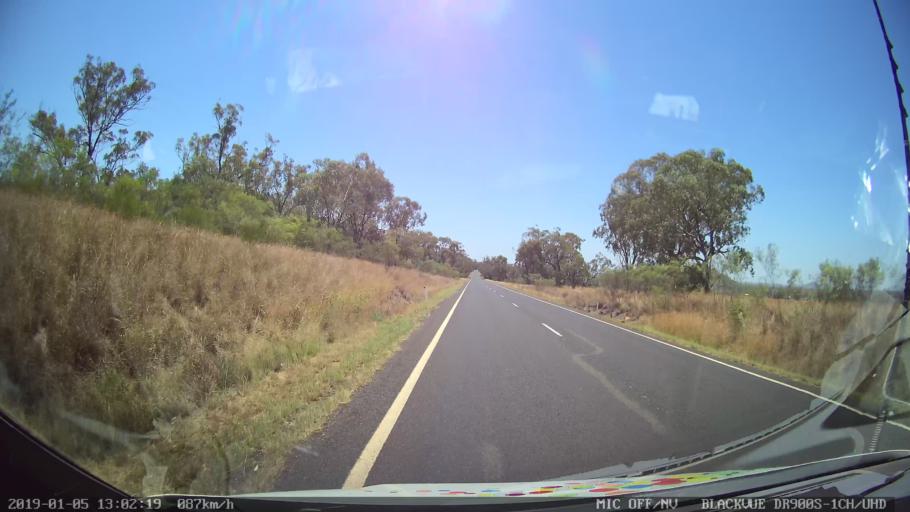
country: AU
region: New South Wales
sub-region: Narrabri
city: Boggabri
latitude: -31.1155
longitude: 149.8100
